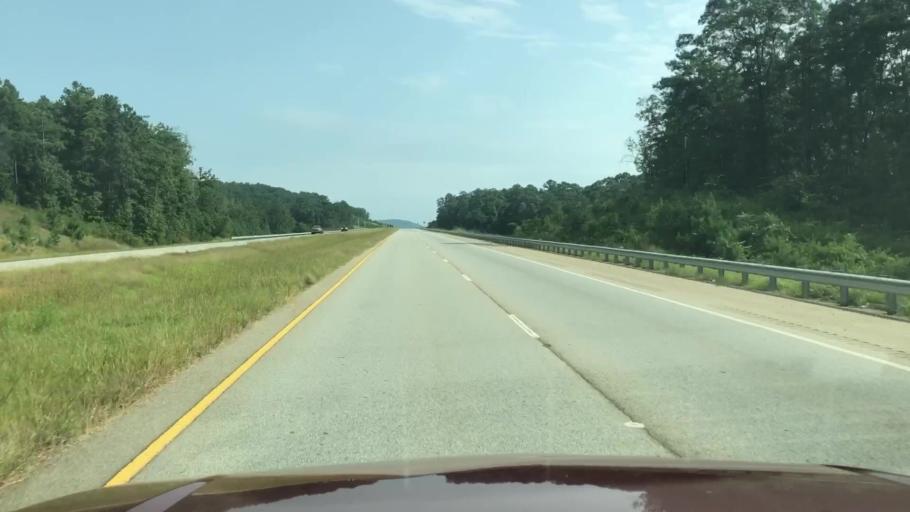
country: US
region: Georgia
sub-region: Bartow County
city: Emerson
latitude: 34.1230
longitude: -84.7662
